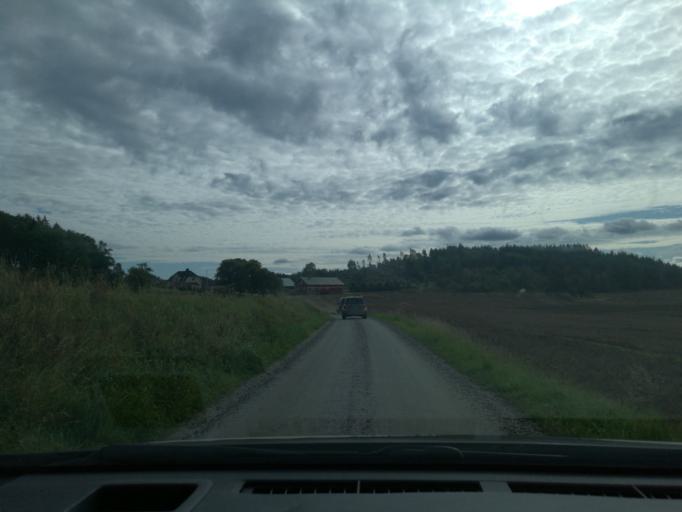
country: SE
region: OEstergoetland
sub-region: Soderkopings Kommun
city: Soederkoeping
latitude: 58.4948
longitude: 16.4713
